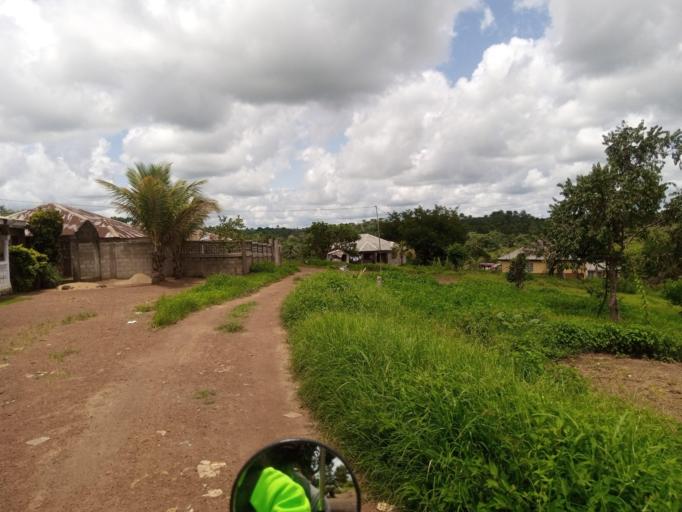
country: SL
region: Northern Province
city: Port Loko
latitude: 8.7587
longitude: -12.7765
